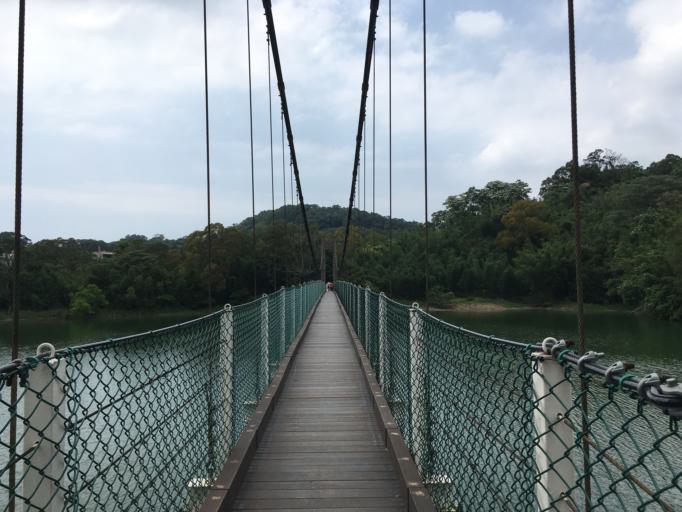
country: TW
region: Taiwan
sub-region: Hsinchu
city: Hsinchu
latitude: 24.7484
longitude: 121.0470
